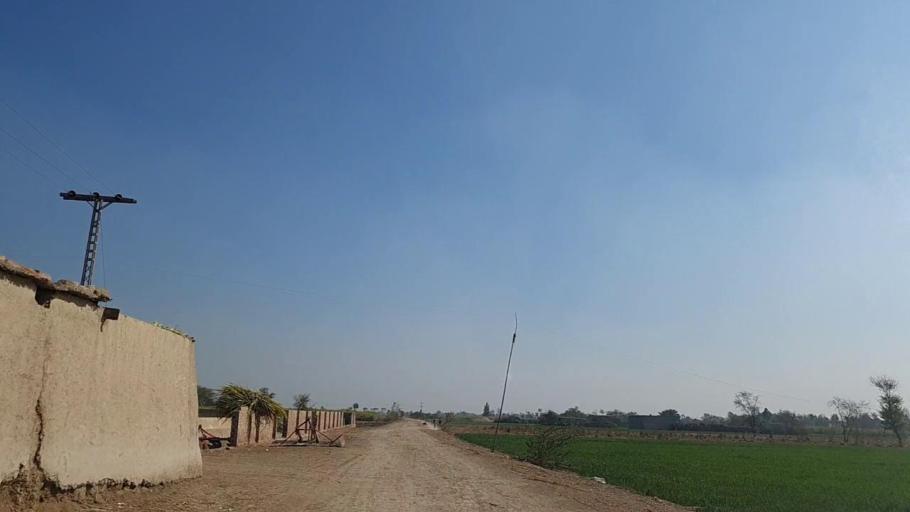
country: PK
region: Sindh
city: Daur
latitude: 26.4820
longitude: 68.3343
